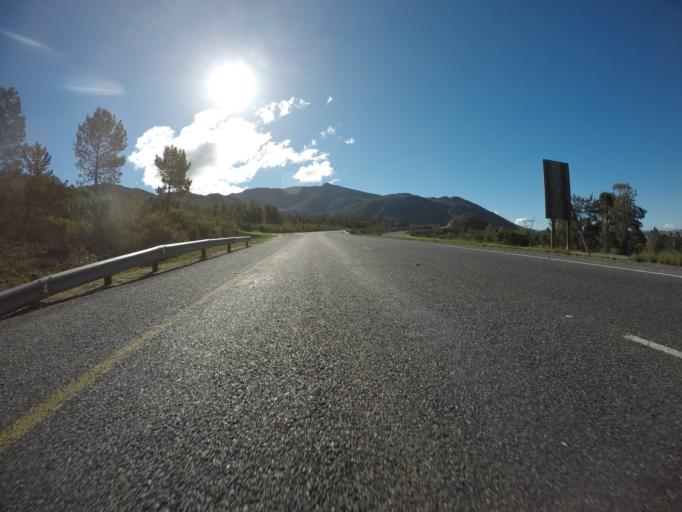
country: ZA
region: Western Cape
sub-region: Overberg District Municipality
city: Grabouw
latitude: -34.2232
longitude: 19.1877
